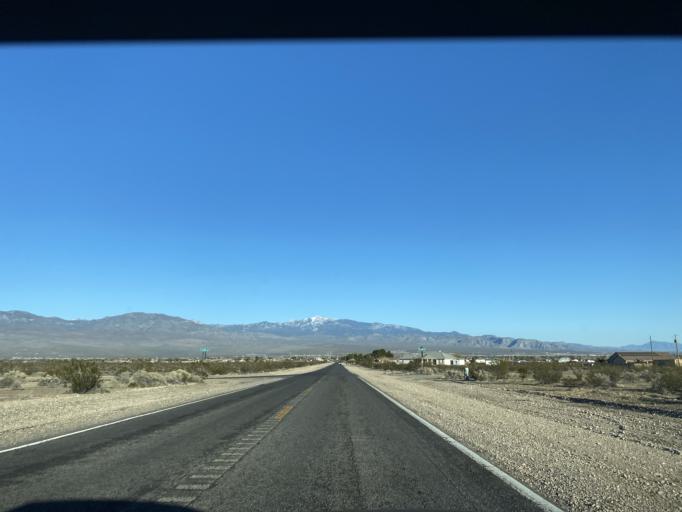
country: US
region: Nevada
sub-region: Nye County
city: Pahrump
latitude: 36.2636
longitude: -116.0955
